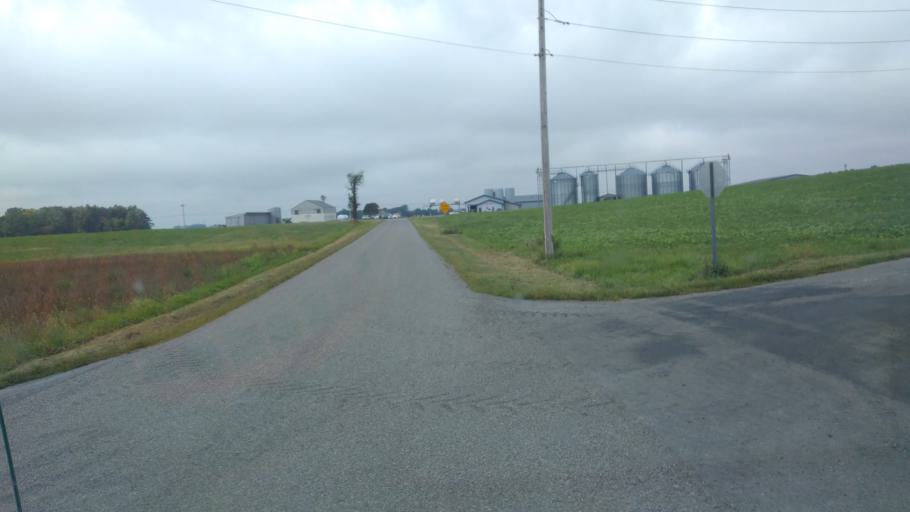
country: US
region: Ohio
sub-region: Hardin County
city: Kenton
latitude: 40.5774
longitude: -83.6826
